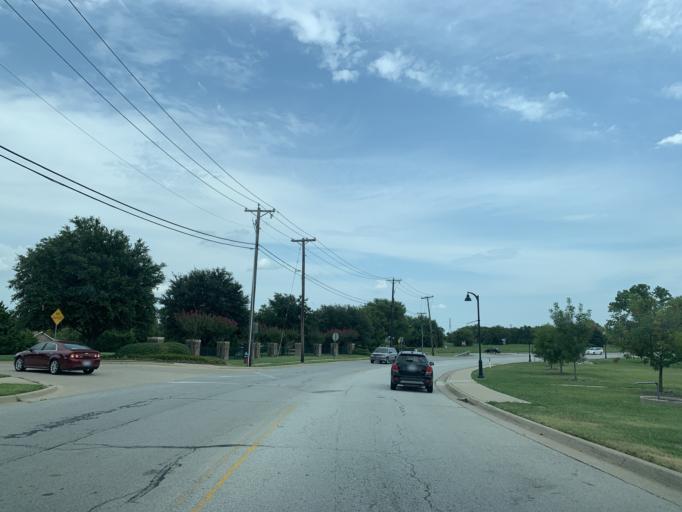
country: US
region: Texas
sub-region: Tarrant County
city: Watauga
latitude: 32.8352
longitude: -97.2728
